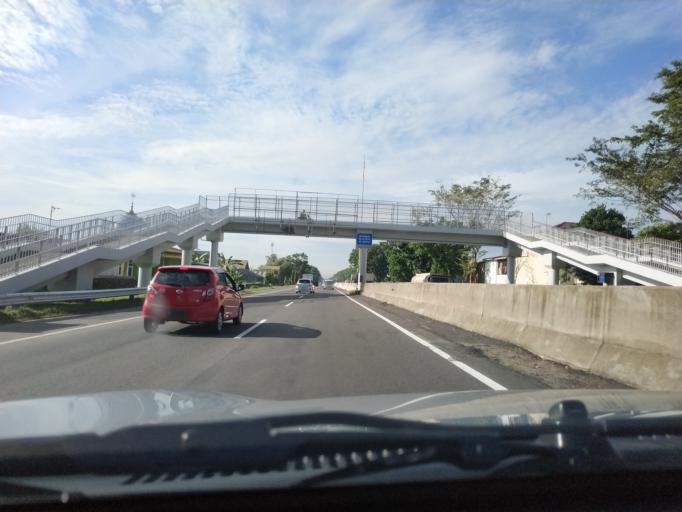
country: ID
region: North Sumatra
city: Medan
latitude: 3.5660
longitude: 98.7259
